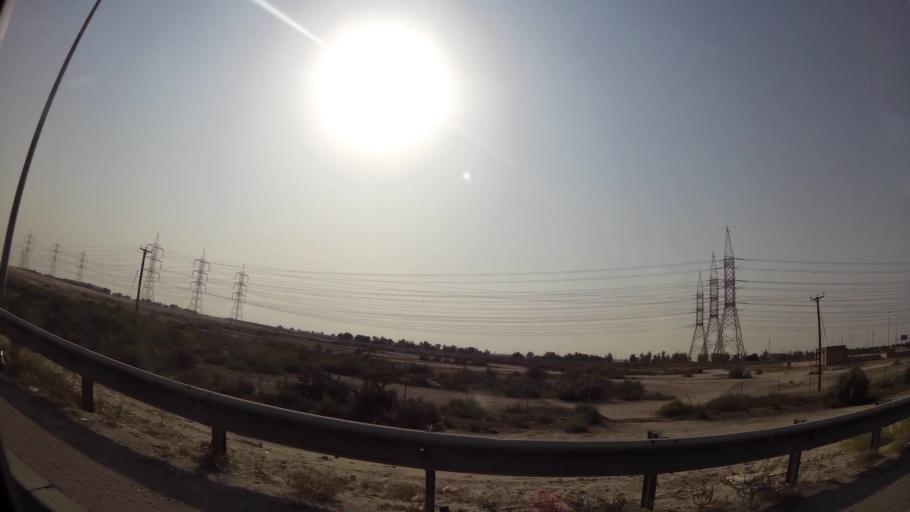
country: KW
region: Muhafazat al Jahra'
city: Al Jahra'
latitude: 29.3094
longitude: 47.7835
